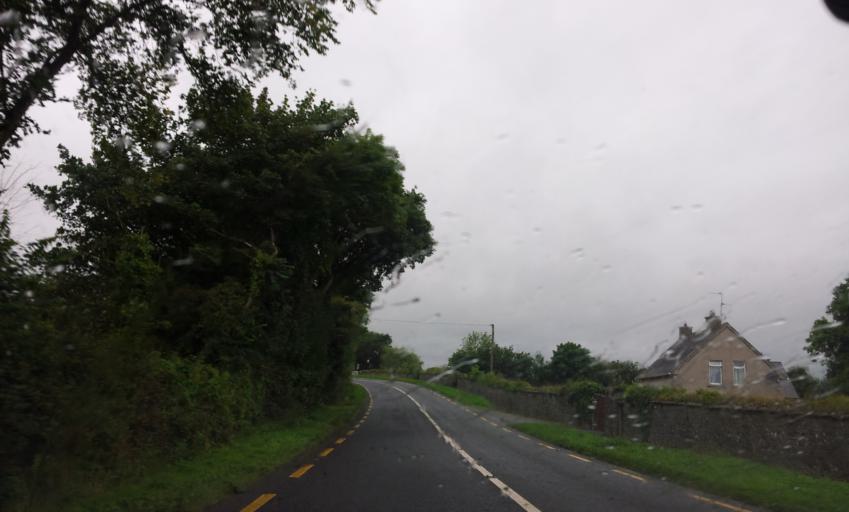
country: IE
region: Munster
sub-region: County Cork
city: Mitchelstown
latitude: 52.2654
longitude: -8.2930
